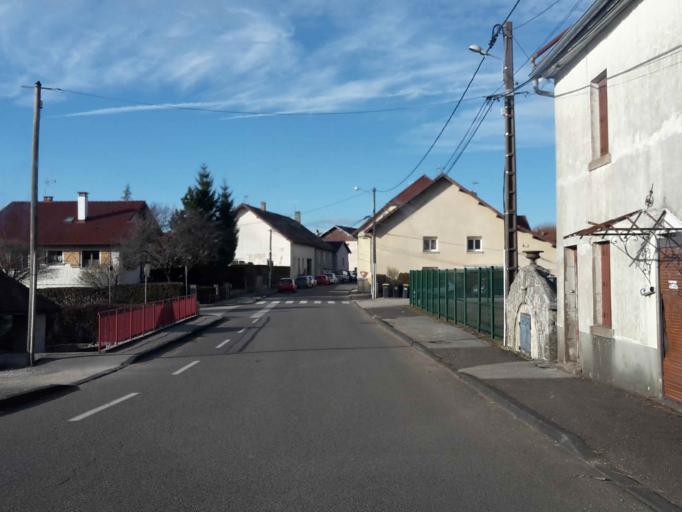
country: FR
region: Franche-Comte
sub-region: Departement du Doubs
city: Vercel-Villedieu-le-Camp
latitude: 47.1808
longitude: 6.3987
